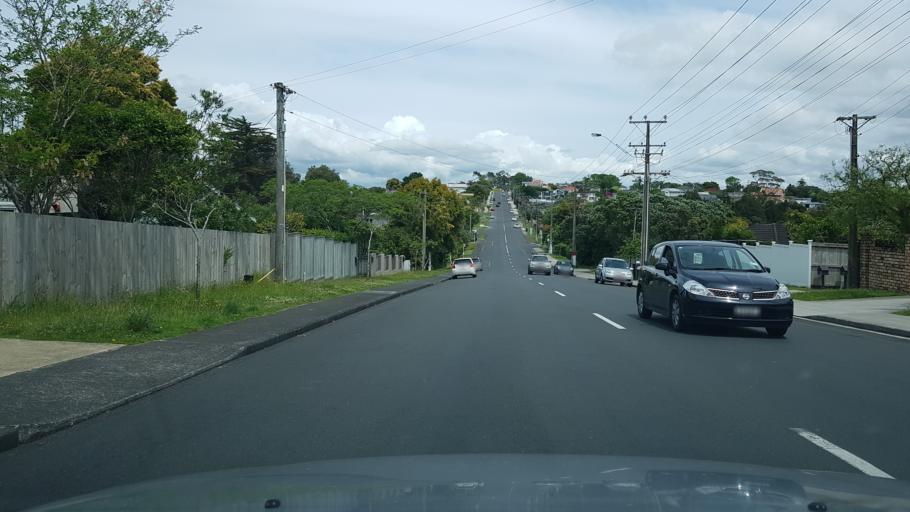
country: NZ
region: Auckland
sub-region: Auckland
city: North Shore
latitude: -36.8020
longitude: 174.7324
